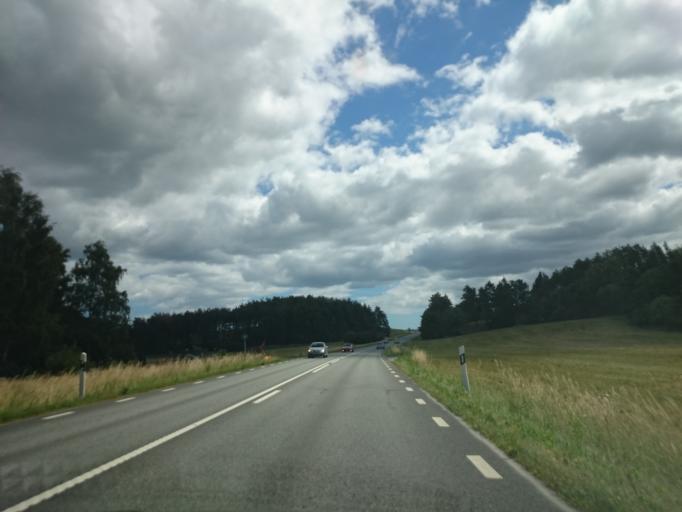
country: SE
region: Skane
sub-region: Kristianstads Kommun
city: Degeberga
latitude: 55.8258
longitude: 14.1008
